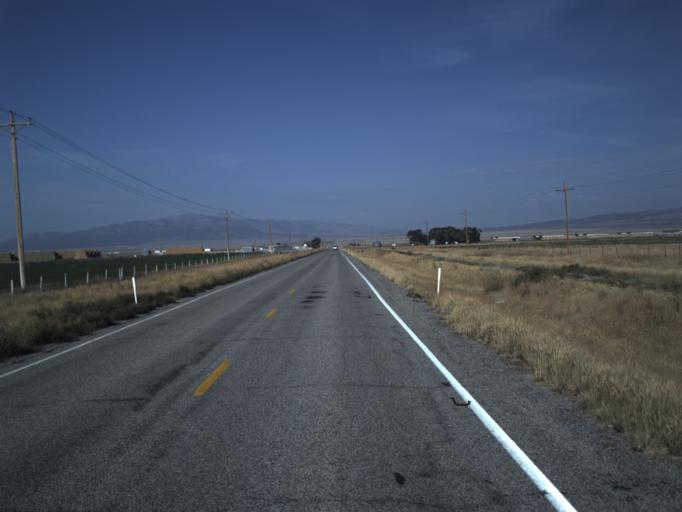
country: US
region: Idaho
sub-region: Oneida County
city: Malad City
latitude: 41.9668
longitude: -112.8844
